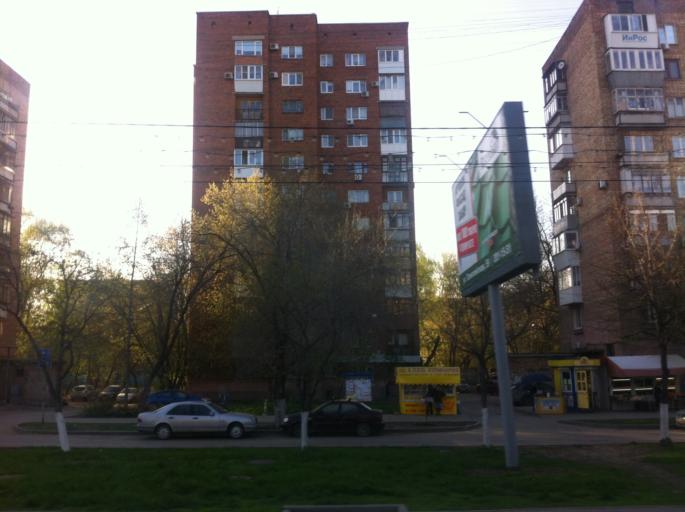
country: RU
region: Samara
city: Samara
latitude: 53.2063
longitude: 50.1319
